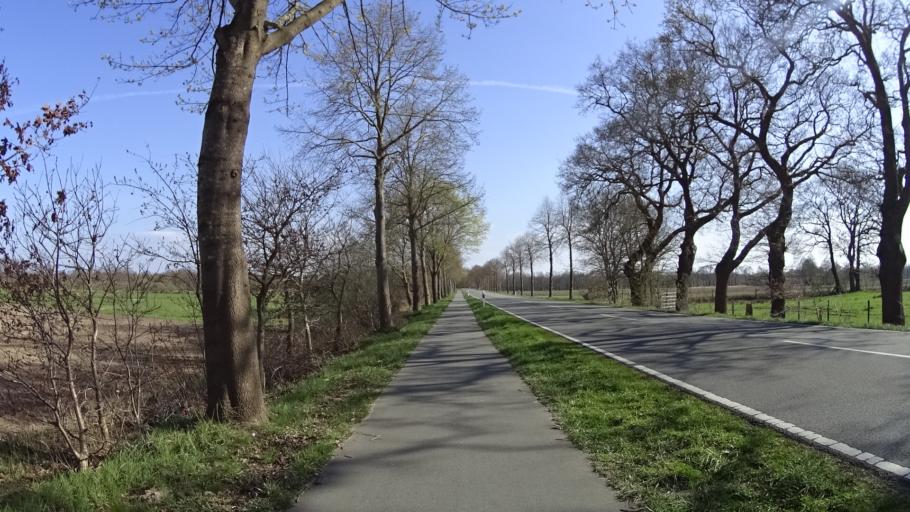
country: DE
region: Lower Saxony
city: Dorpen
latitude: 52.9740
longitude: 7.3116
